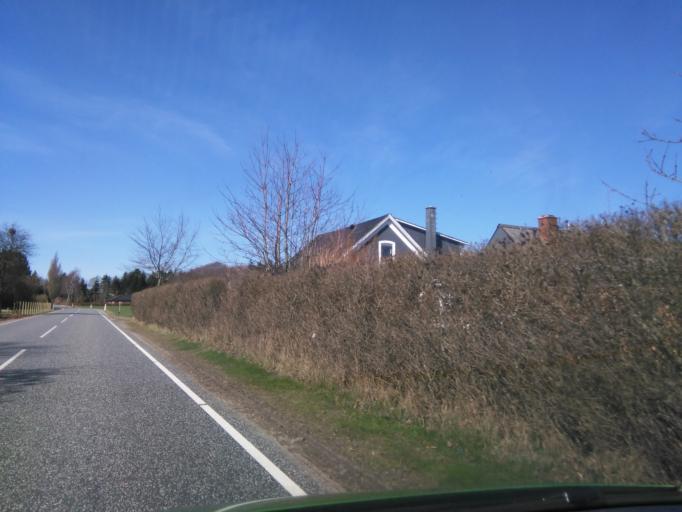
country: DK
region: Central Jutland
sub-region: Skanderborg Kommune
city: Ry
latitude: 56.0237
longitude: 9.7478
